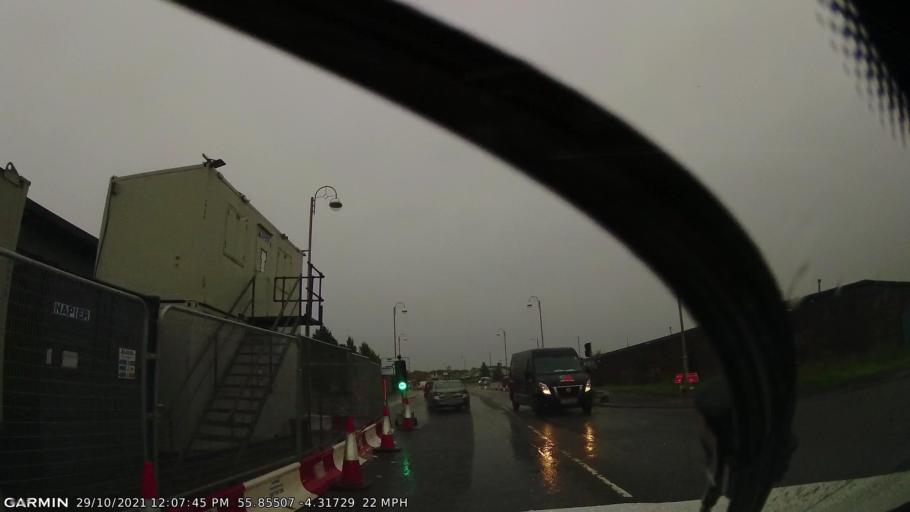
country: GB
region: Scotland
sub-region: East Renfrewshire
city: Giffnock
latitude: 55.8550
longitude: -4.3173
